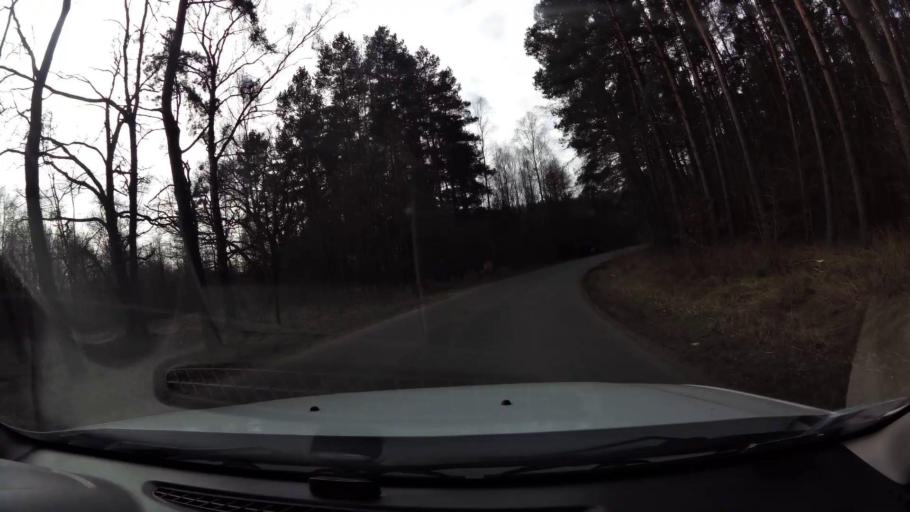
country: PL
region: West Pomeranian Voivodeship
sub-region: Powiat mysliborski
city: Debno
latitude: 52.8363
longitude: 14.6704
